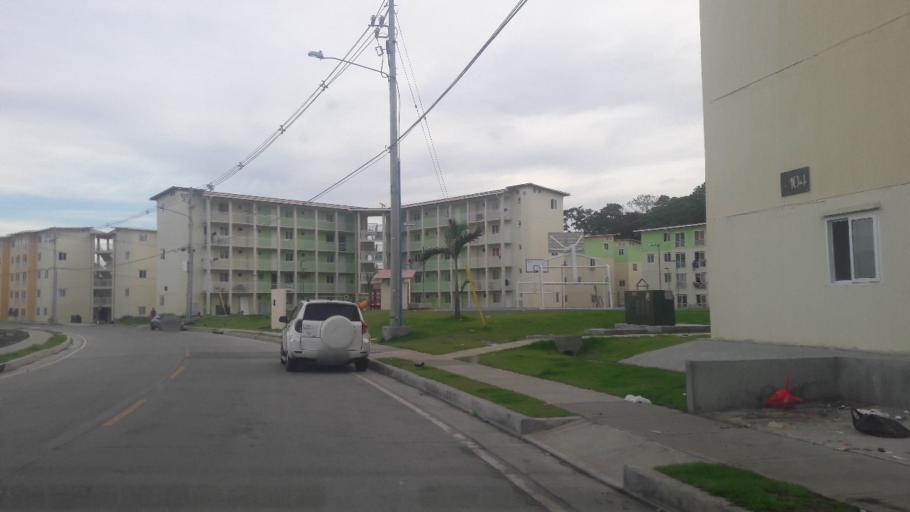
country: PA
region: Colon
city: Cativa
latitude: 9.3700
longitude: -79.8483
